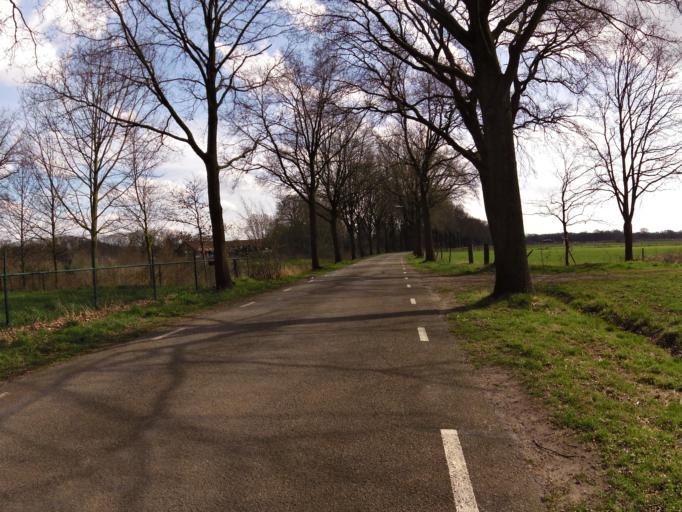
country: NL
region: North Brabant
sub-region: Gemeente Vught
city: Vught
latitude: 51.6483
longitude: 5.2440
